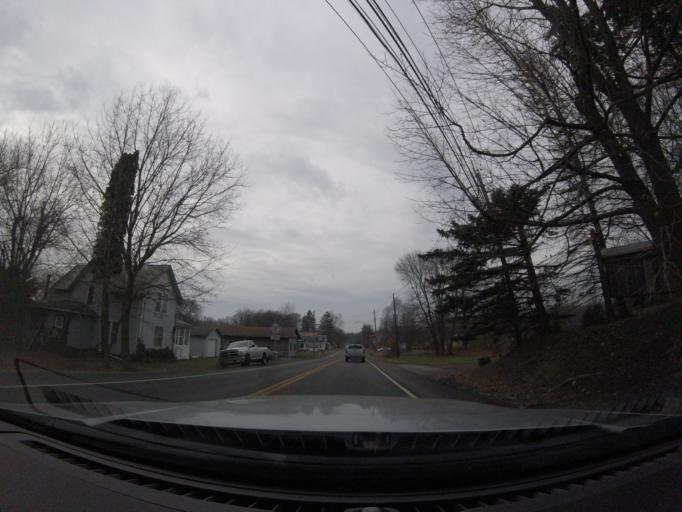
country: US
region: New York
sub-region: Schuyler County
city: Watkins Glen
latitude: 42.4206
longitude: -76.8428
